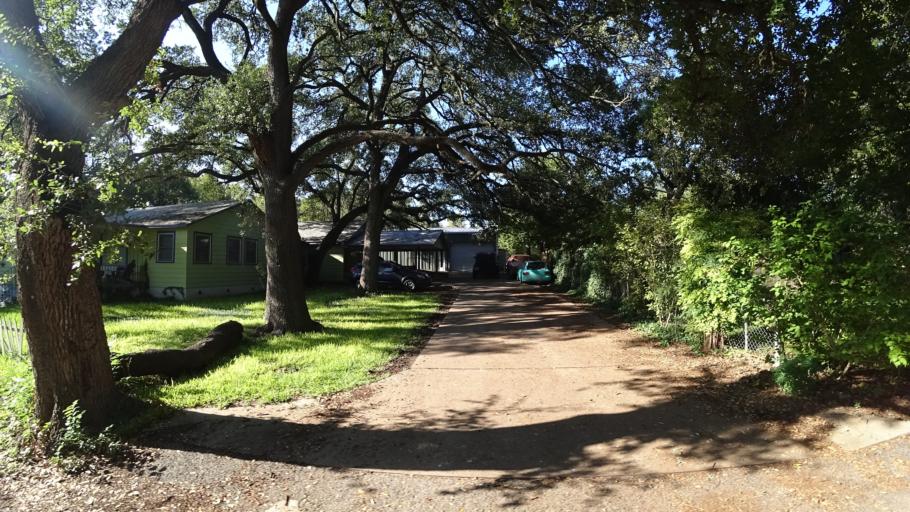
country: US
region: Texas
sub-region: Travis County
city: Wells Branch
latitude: 30.3530
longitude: -97.6977
